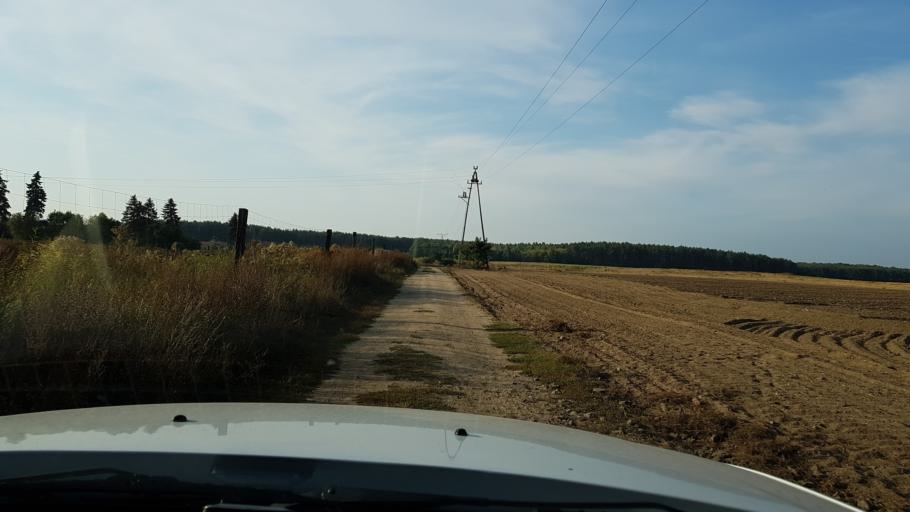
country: PL
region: West Pomeranian Voivodeship
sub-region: Powiat kamienski
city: Wolin
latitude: 53.8414
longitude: 14.6057
